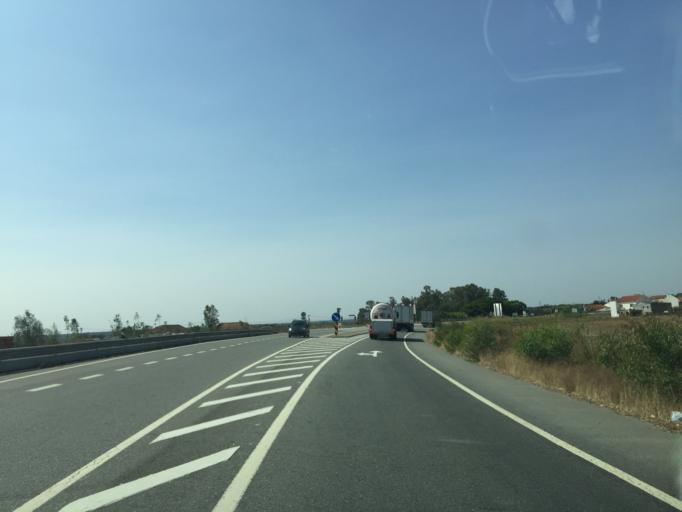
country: PT
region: Beja
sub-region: Aljustrel
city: Aljustrel
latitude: 37.9424
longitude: -8.3780
